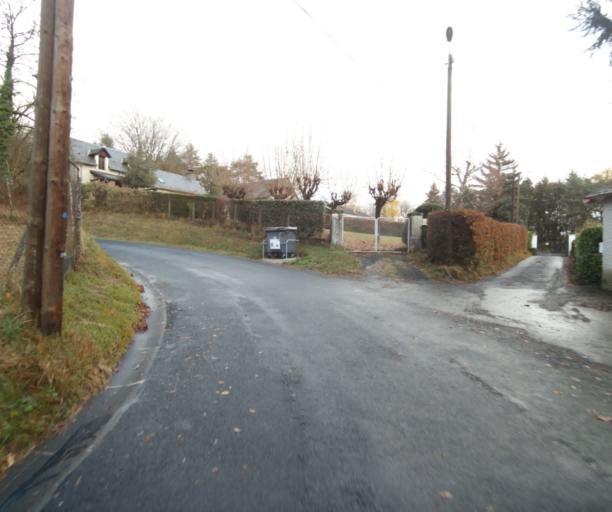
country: FR
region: Limousin
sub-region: Departement de la Correze
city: Cornil
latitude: 45.2212
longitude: 1.6941
